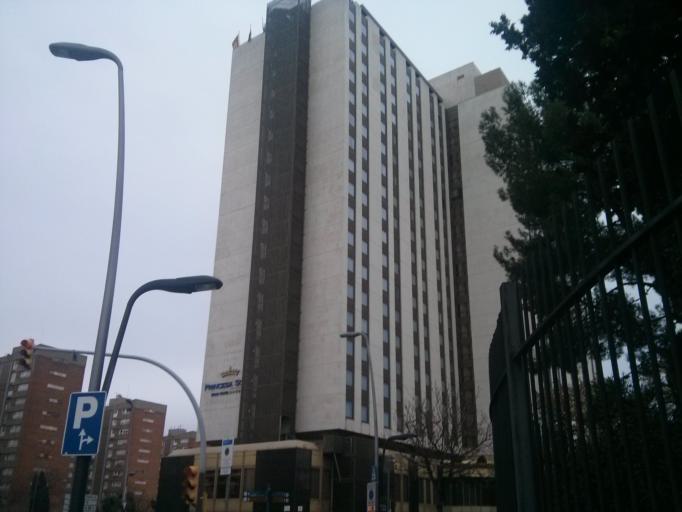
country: ES
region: Catalonia
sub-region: Provincia de Barcelona
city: les Corts
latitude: 41.3867
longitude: 2.1222
